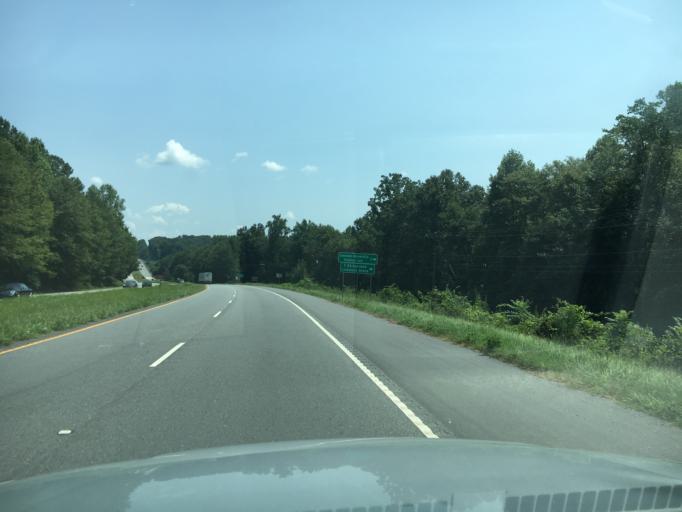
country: US
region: South Carolina
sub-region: Anderson County
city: Pendleton
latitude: 34.6480
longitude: -82.8064
